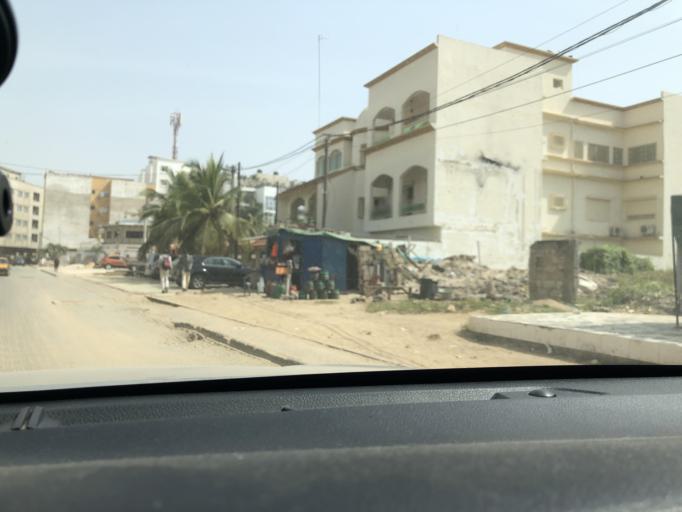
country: SN
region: Dakar
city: Mermoz Boabab
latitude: 14.7444
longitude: -17.5141
